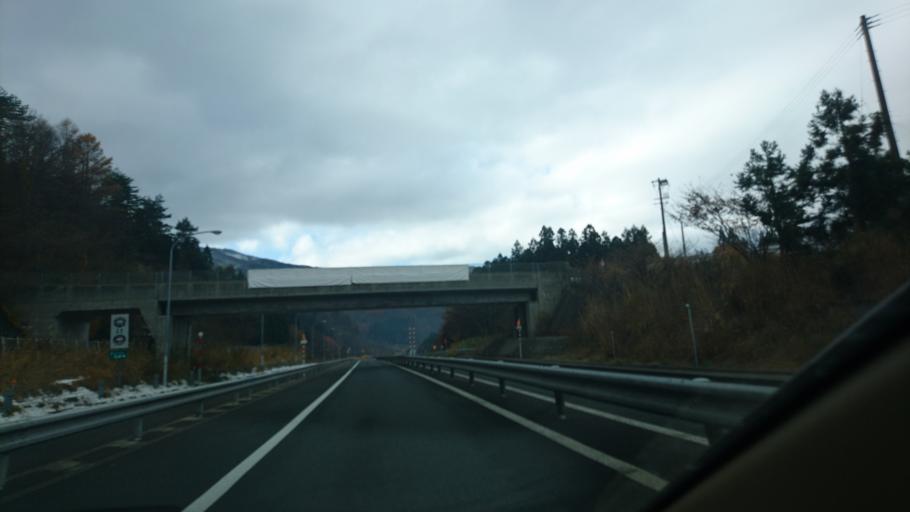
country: JP
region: Iwate
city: Kitakami
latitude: 39.2974
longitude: 140.9344
